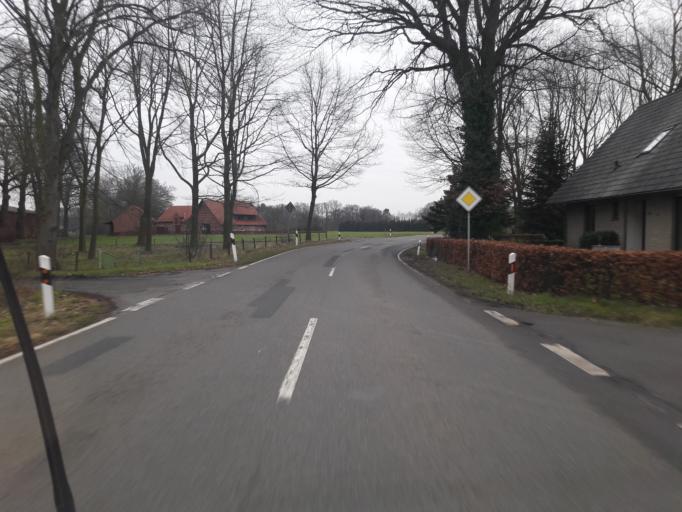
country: DE
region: Lower Saxony
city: Warmsen
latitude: 52.4244
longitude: 8.8557
